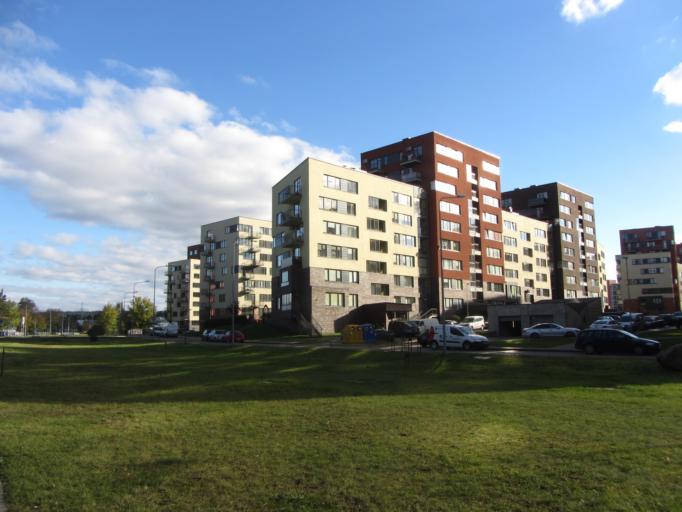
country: LT
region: Vilnius County
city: Lazdynai
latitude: 54.6693
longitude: 25.2119
